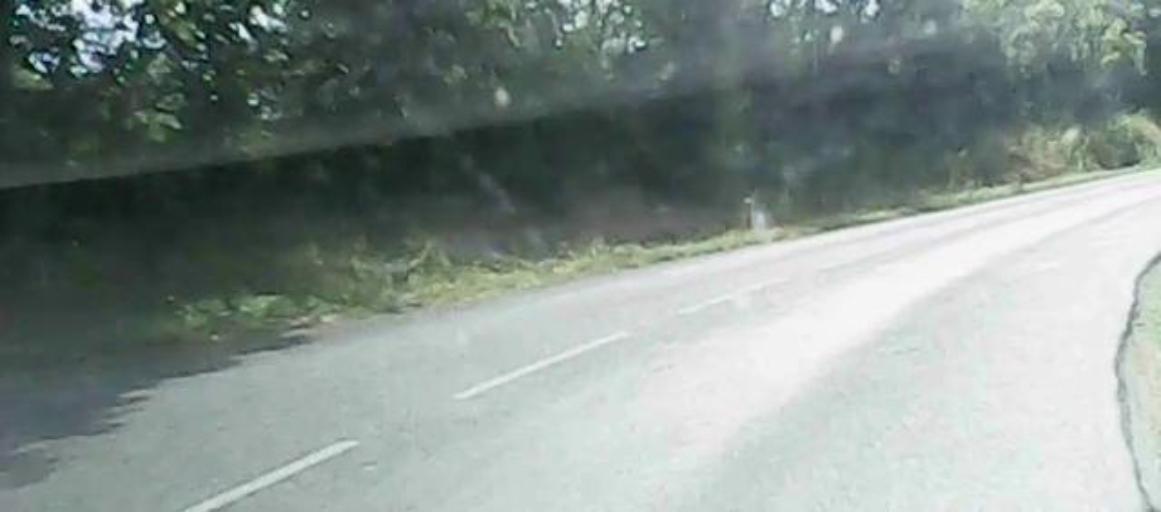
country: FR
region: Auvergne
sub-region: Departement de l'Allier
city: Saint-Yorre
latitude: 46.0649
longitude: 3.4850
